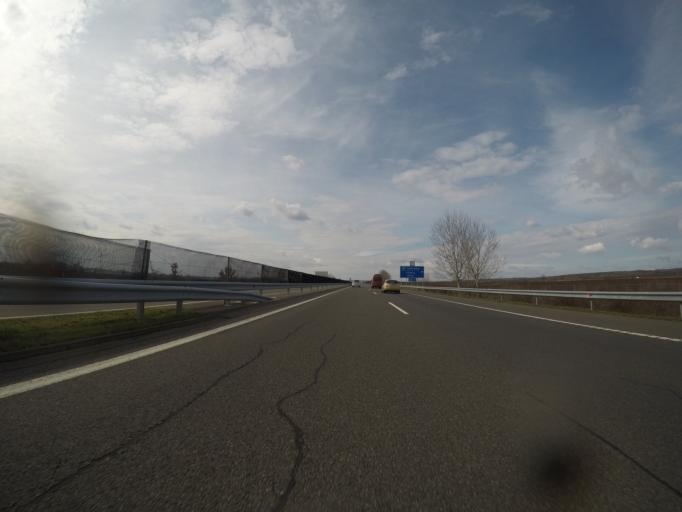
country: HU
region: Baranya
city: Boly
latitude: 45.9846
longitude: 18.5122
